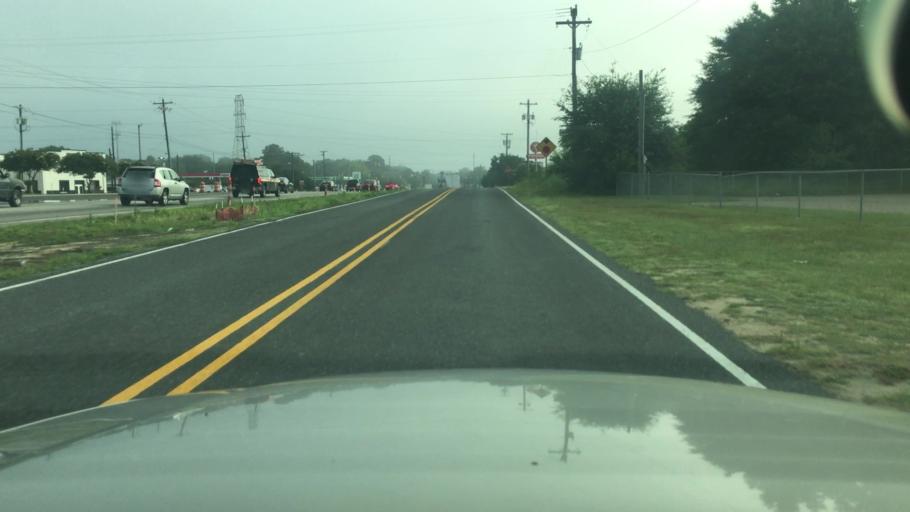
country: US
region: North Carolina
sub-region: Cumberland County
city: Fayetteville
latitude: 35.0172
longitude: -78.8962
